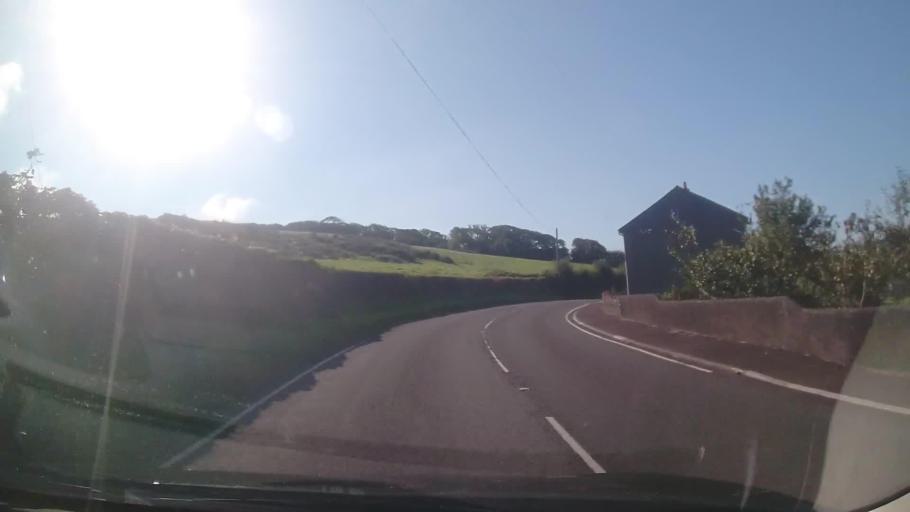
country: GB
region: England
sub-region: Cumbria
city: Seascale
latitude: 54.3253
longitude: -3.3753
